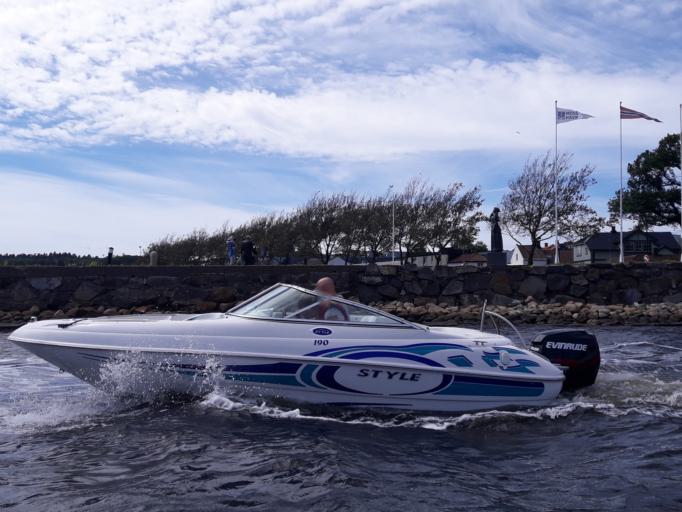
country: NO
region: Ostfold
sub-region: Moss
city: Moss
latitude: 59.4313
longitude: 10.6531
